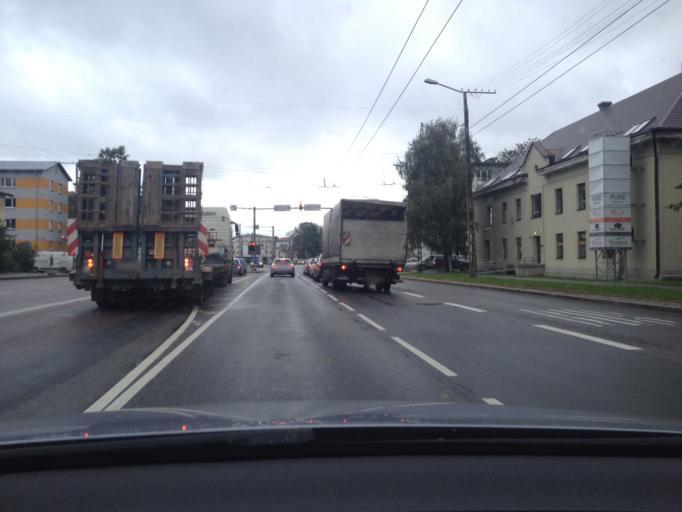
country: EE
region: Harju
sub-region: Tallinna linn
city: Tallinn
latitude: 59.4255
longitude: 24.7180
